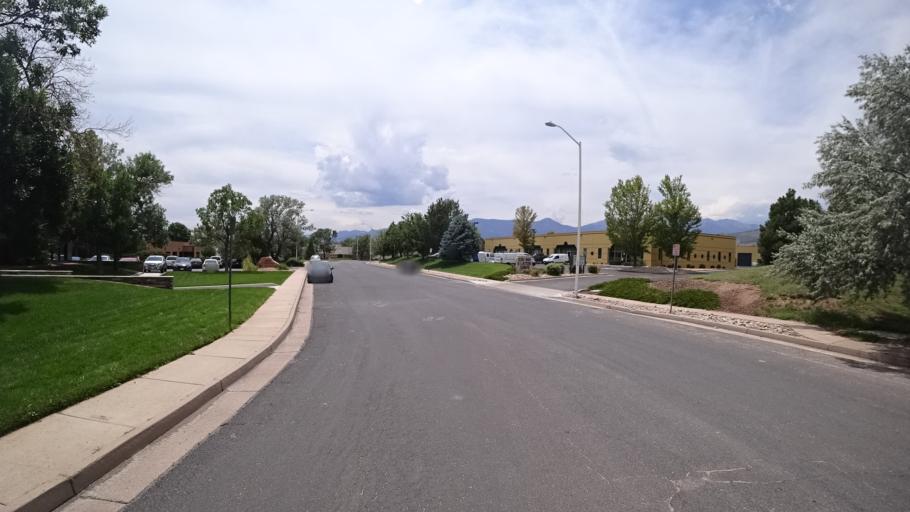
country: US
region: Colorado
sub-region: El Paso County
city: Colorado Springs
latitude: 38.9014
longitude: -104.8431
